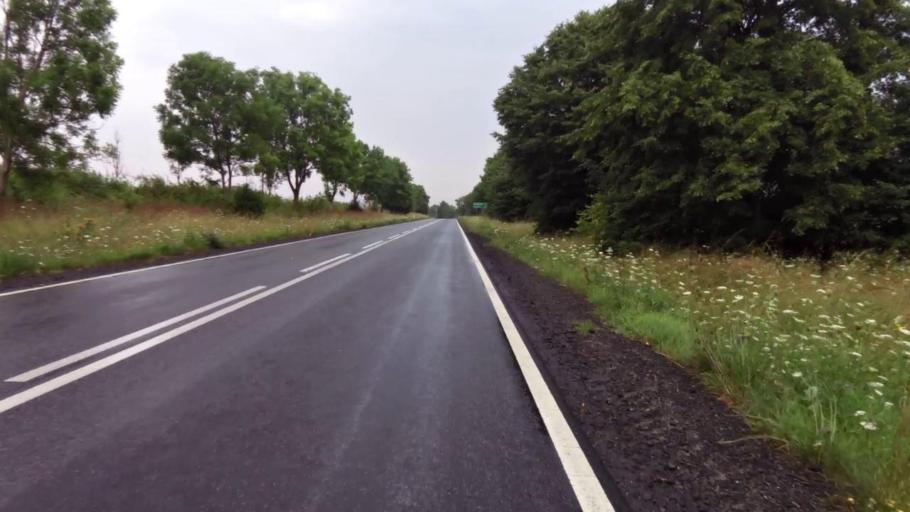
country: PL
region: West Pomeranian Voivodeship
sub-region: Powiat stargardzki
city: Insko
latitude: 53.4493
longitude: 15.5722
